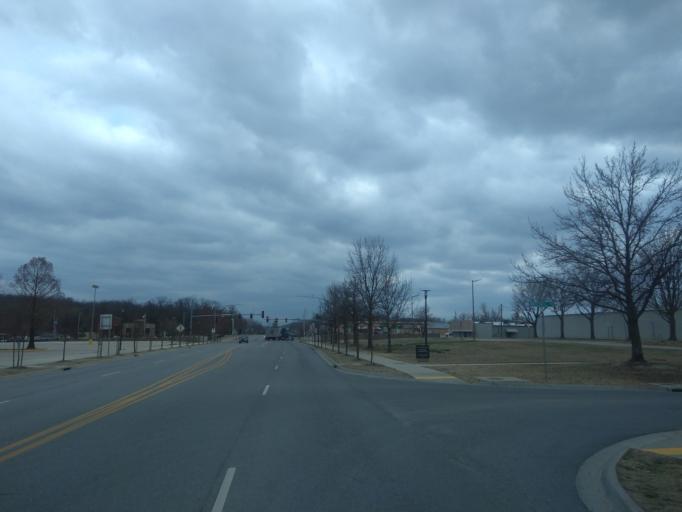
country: US
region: Arkansas
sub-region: Washington County
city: Fayetteville
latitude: 36.0582
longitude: -94.1805
